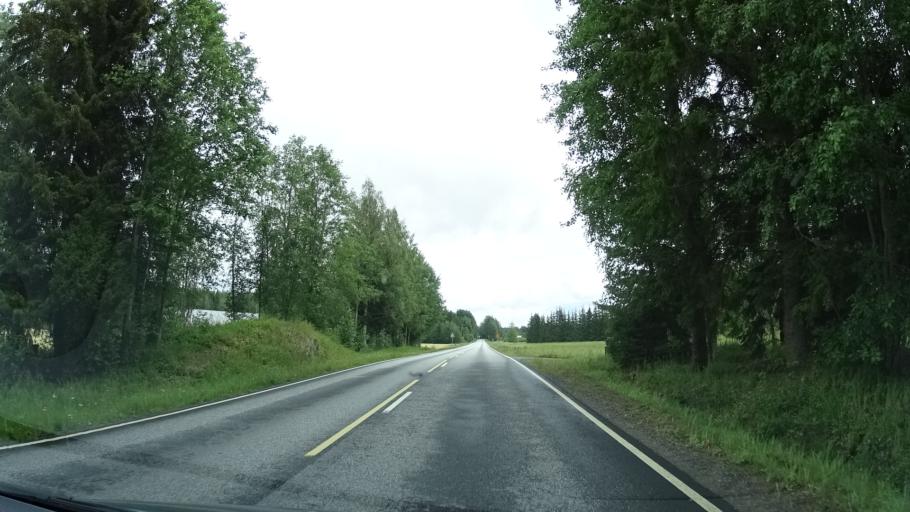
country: FI
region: Haeme
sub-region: Forssa
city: Humppila
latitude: 61.0956
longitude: 23.3607
